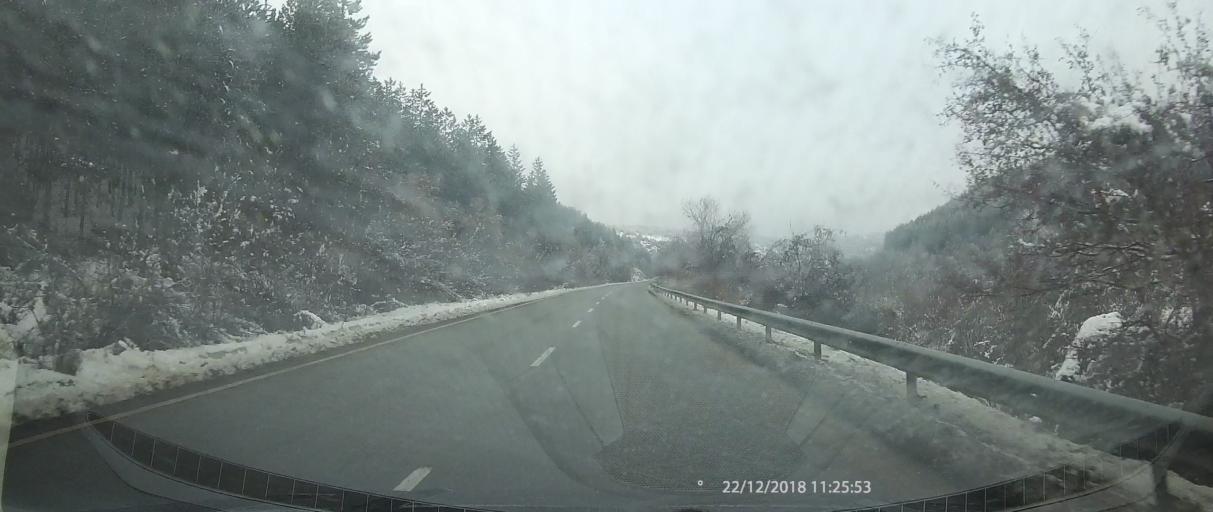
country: BG
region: Kyustendil
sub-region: Obshtina Boboshevo
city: Boboshevo
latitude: 42.2589
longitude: 22.9164
